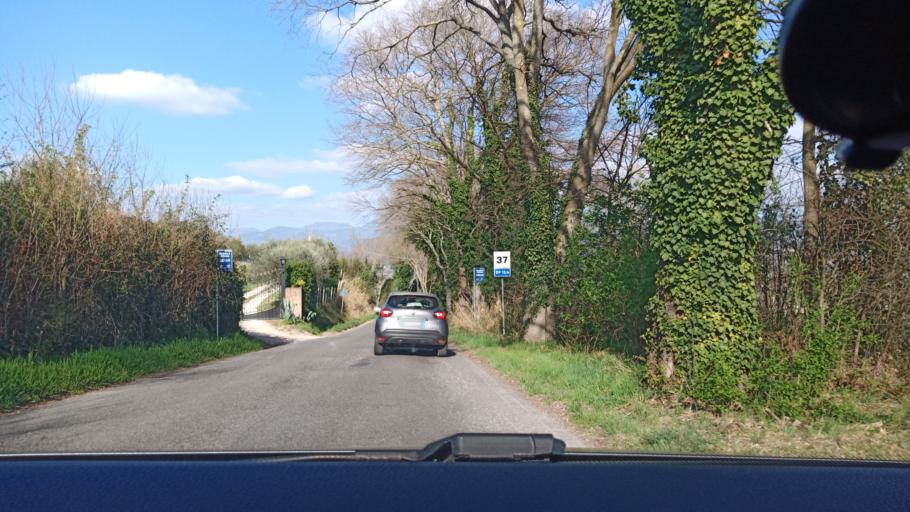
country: IT
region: Latium
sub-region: Citta metropolitana di Roma Capitale
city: Torrita Tiberina
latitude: 42.2423
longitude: 12.6177
